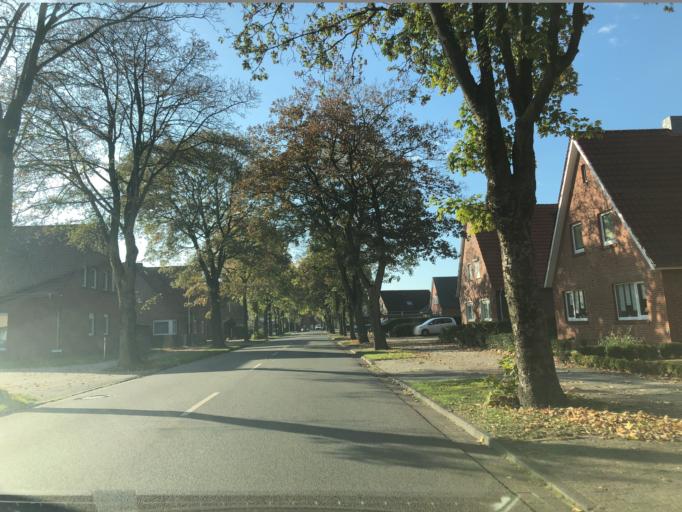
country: DE
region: Lower Saxony
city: Papenburg
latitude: 53.0779
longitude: 7.4277
